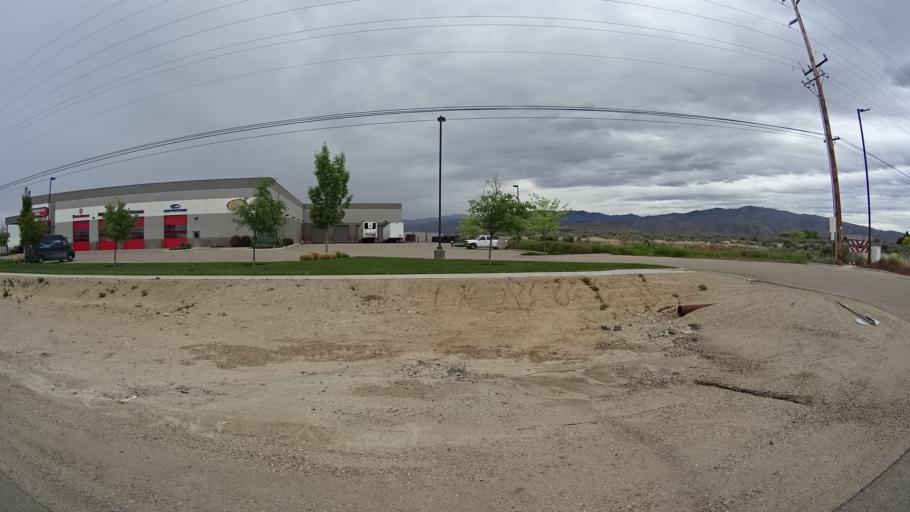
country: US
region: Idaho
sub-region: Ada County
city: Boise
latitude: 43.5447
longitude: -116.1762
